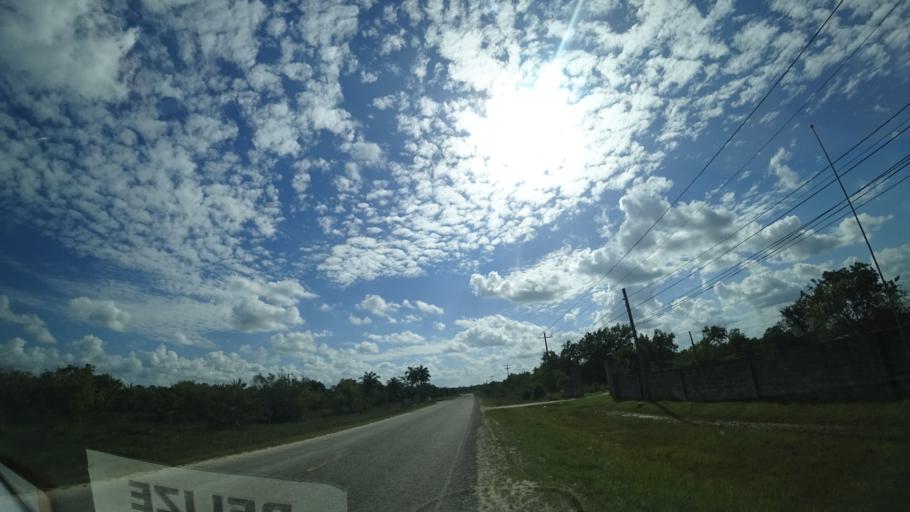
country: BZ
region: Belize
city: Belize City
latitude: 17.5575
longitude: -88.4061
